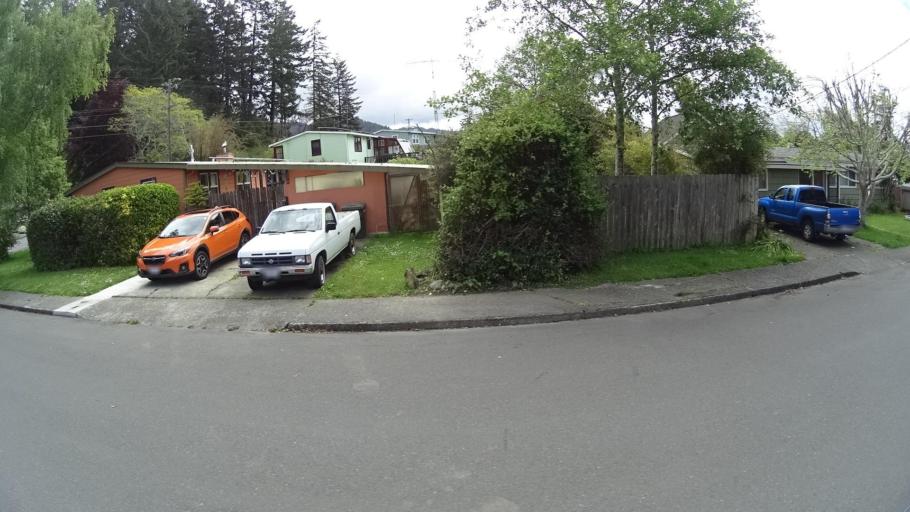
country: US
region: California
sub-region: Humboldt County
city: Arcata
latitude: 40.8599
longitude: -124.0680
